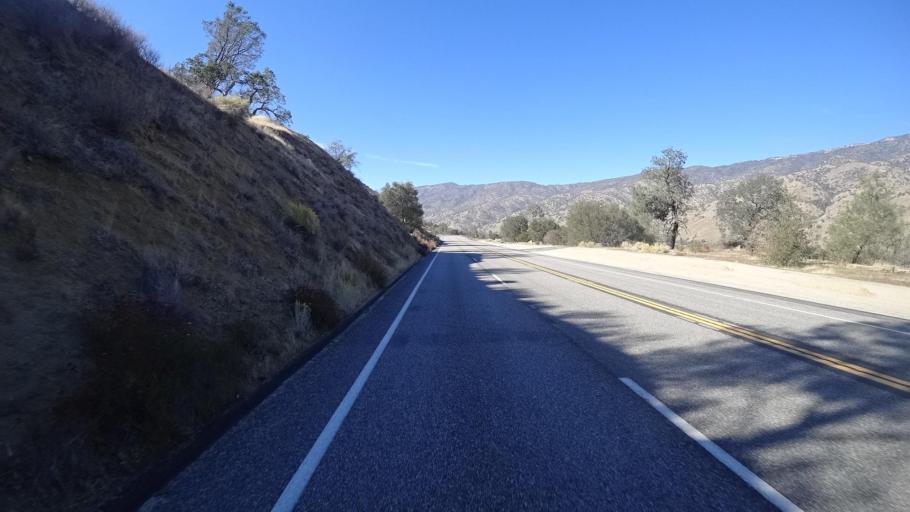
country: US
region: California
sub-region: Kern County
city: Bodfish
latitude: 35.5308
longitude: -118.6367
